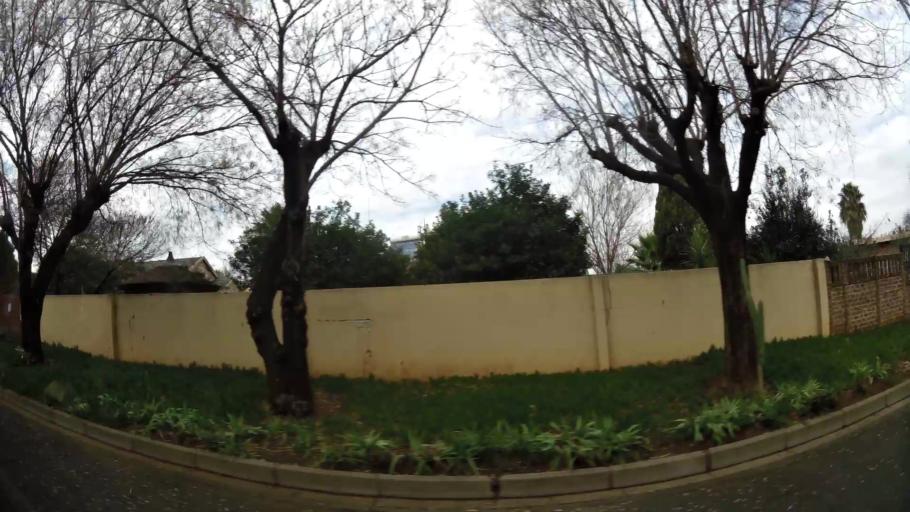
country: ZA
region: Gauteng
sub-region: Sedibeng District Municipality
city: Vereeniging
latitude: -26.6425
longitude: 27.9777
